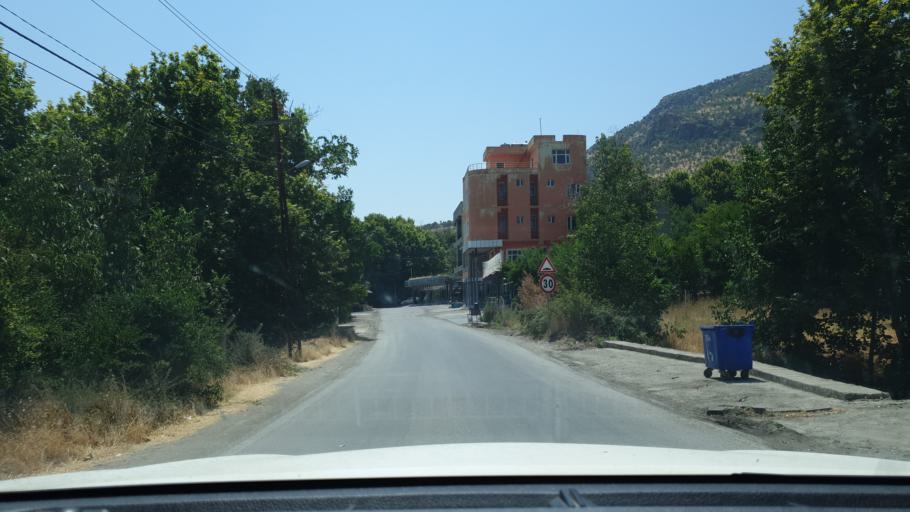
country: IQ
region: Arbil
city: Nahiyat Hiran
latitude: 36.2808
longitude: 44.4948
